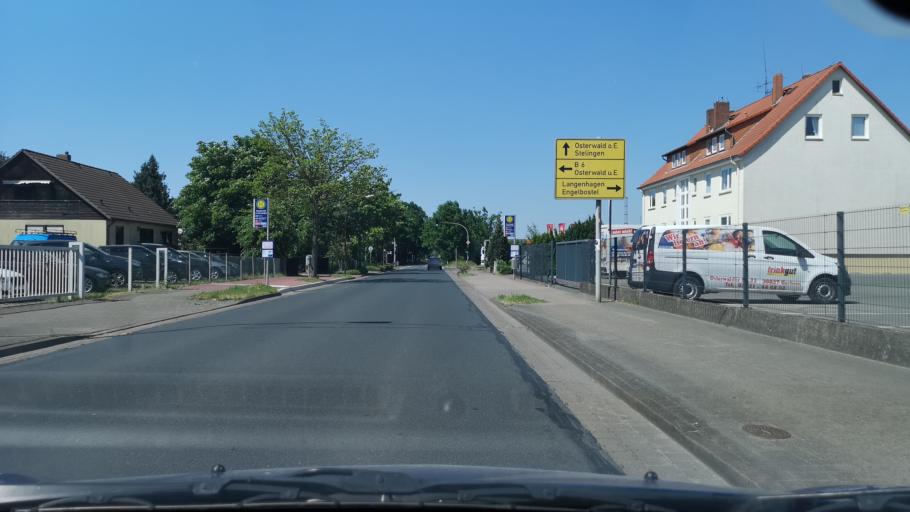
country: DE
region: Lower Saxony
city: Garbsen-Mitte
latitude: 52.4458
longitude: 9.6081
